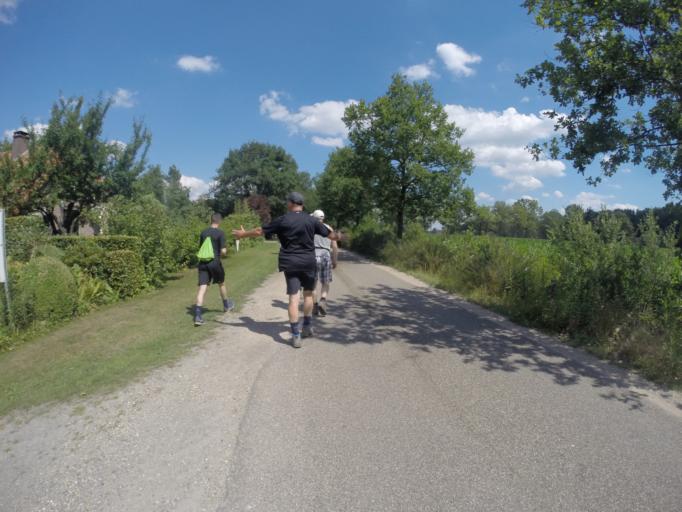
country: NL
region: Gelderland
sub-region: Gemeente Lochem
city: Barchem
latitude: 52.1128
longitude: 6.4350
